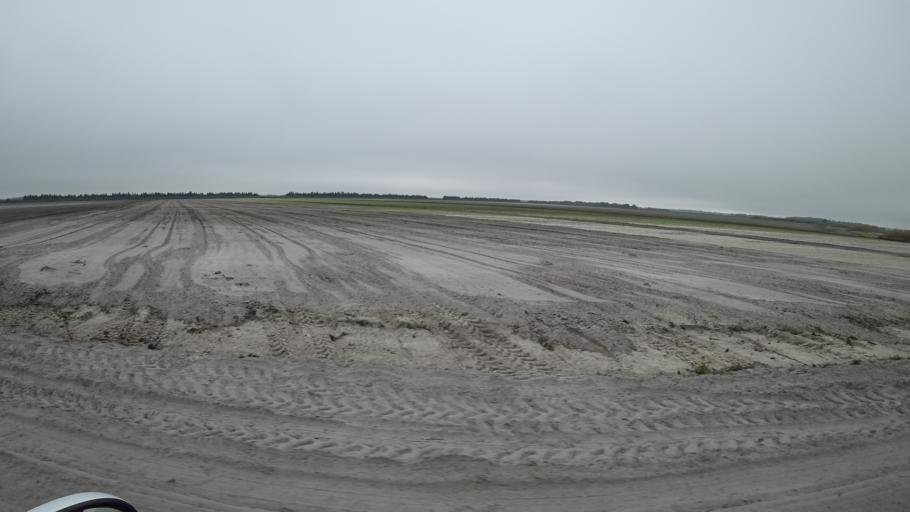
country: US
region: Florida
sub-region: Sarasota County
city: Warm Mineral Springs
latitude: 27.3036
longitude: -82.1602
